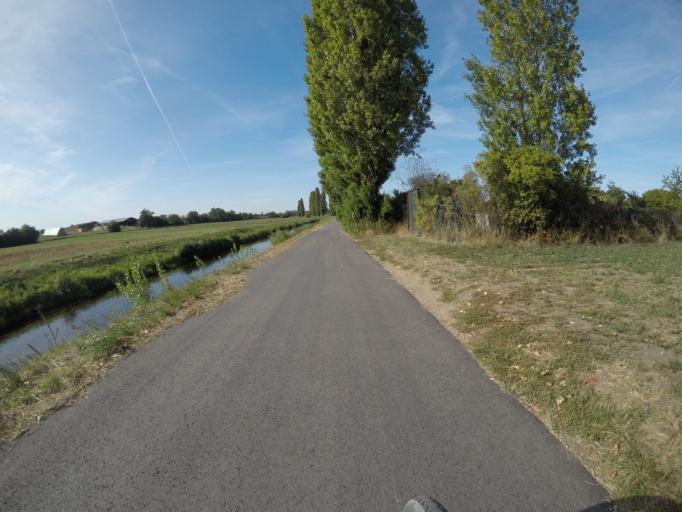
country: DE
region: Baden-Wuerttemberg
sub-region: Karlsruhe Region
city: Reilingen
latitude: 49.3064
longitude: 8.5623
